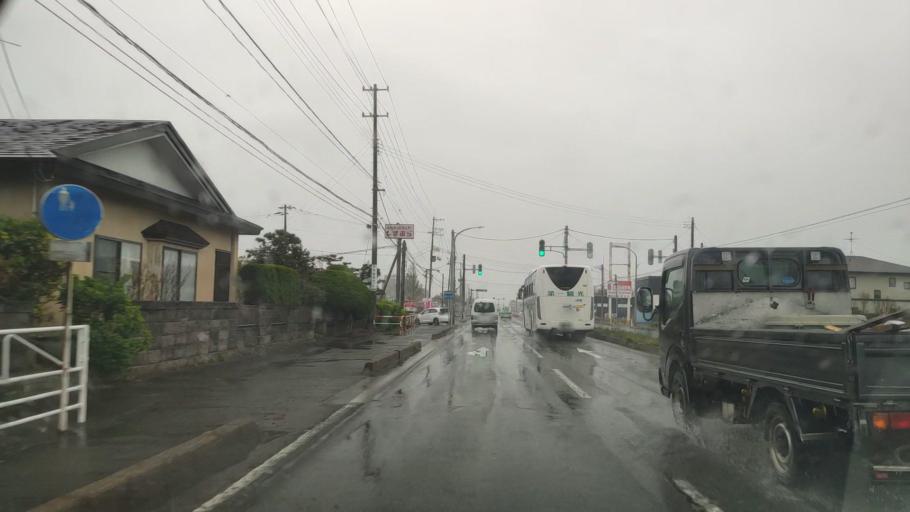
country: JP
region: Akita
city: Tenno
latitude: 39.8825
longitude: 139.9824
